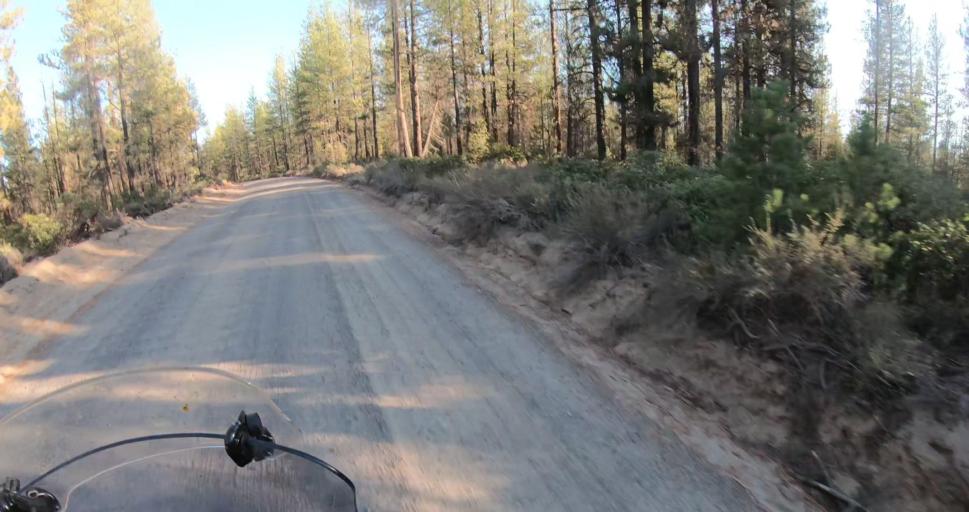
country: US
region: Oregon
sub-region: Deschutes County
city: La Pine
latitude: 43.7157
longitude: -121.3878
